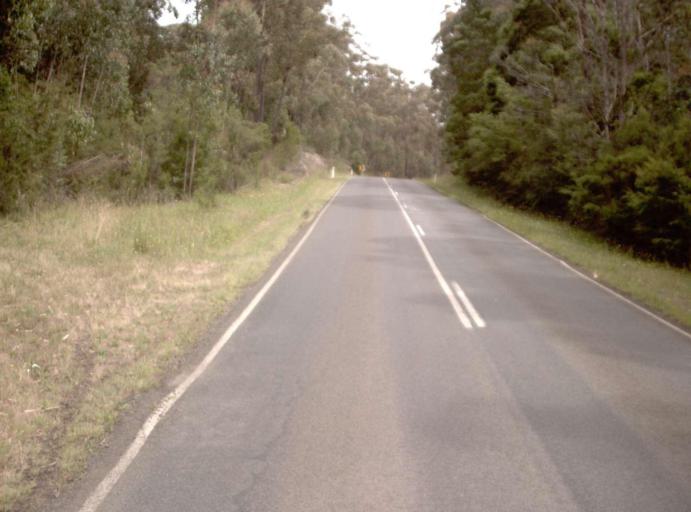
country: AU
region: Victoria
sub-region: Latrobe
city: Morwell
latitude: -38.0802
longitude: 146.4315
